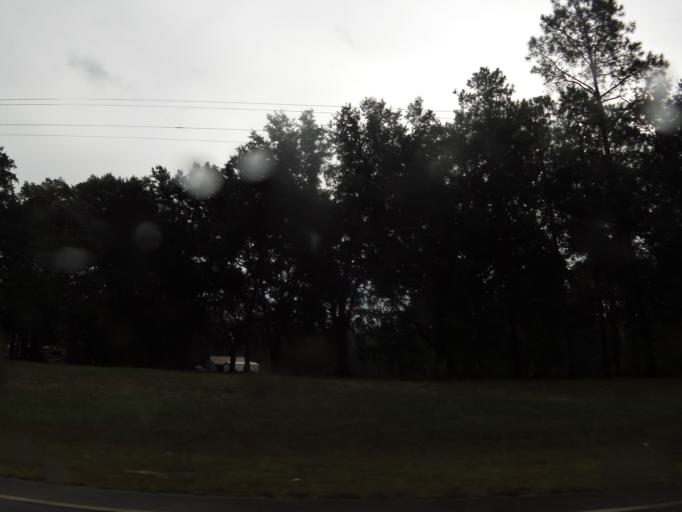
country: US
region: Georgia
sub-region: Wayne County
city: Jesup
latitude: 31.5728
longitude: -81.8842
